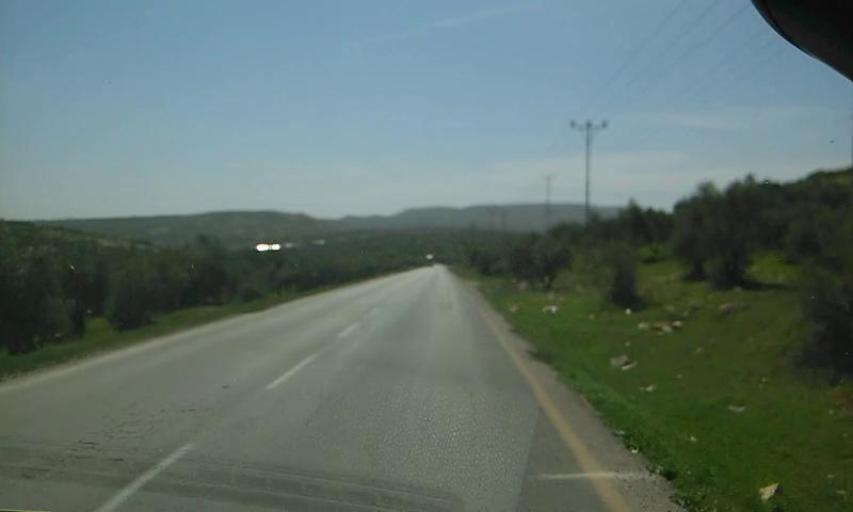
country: PS
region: West Bank
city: Marah Rabbah
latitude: 31.6351
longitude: 35.2027
